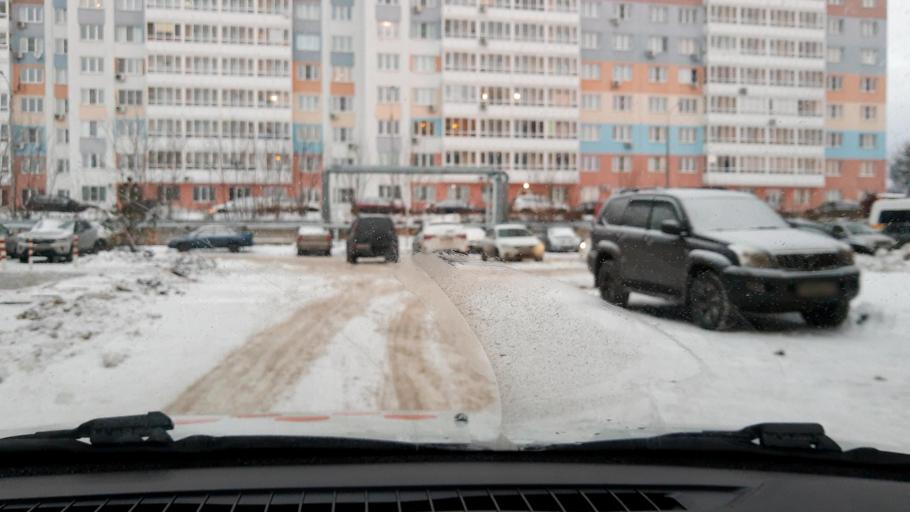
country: RU
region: Nizjnij Novgorod
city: Nizhniy Novgorod
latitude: 56.2837
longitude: 43.9872
